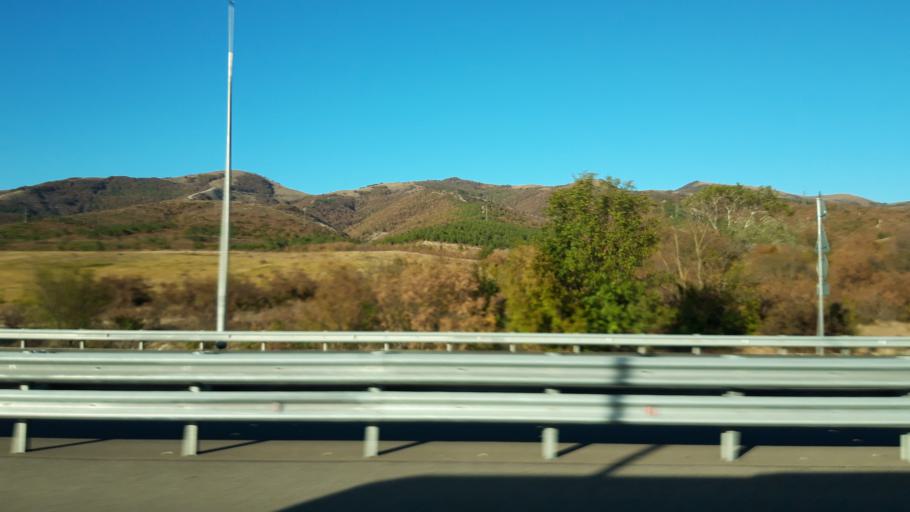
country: RU
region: Krasnodarskiy
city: Kabardinka
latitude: 44.6440
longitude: 37.9685
